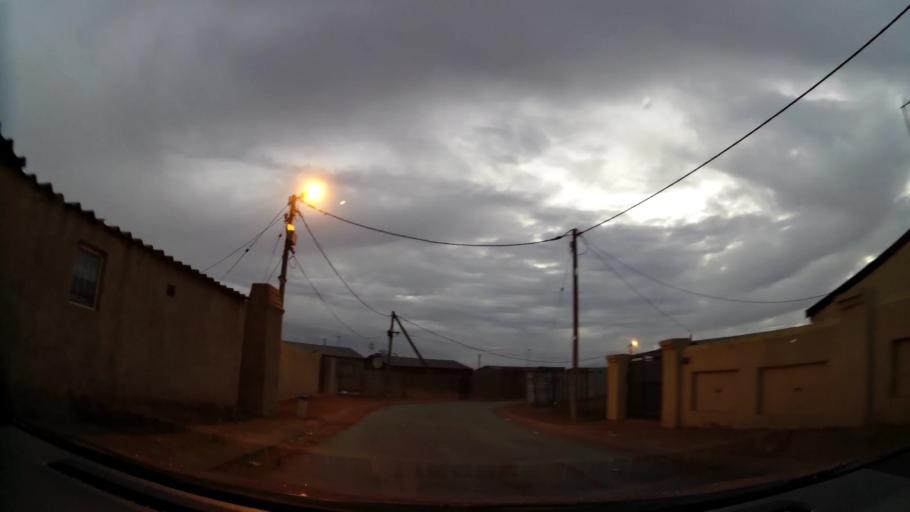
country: ZA
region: Gauteng
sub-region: West Rand District Municipality
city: Randfontein
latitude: -26.1755
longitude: 27.7856
